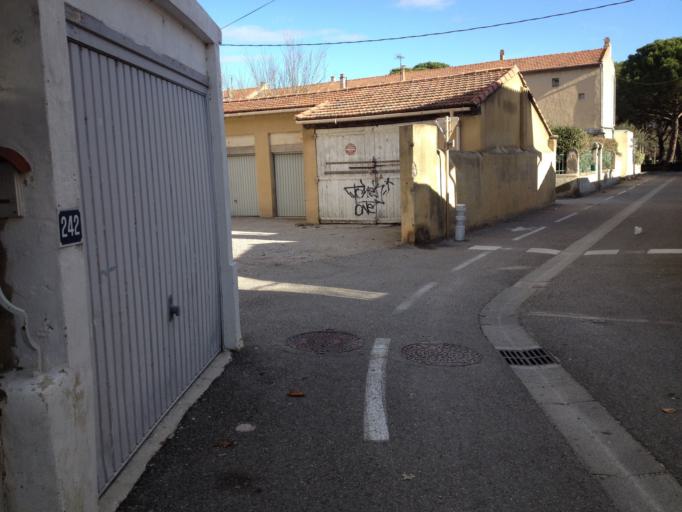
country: FR
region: Provence-Alpes-Cote d'Azur
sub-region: Departement du Vaucluse
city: Orange
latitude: 44.1358
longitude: 4.8132
